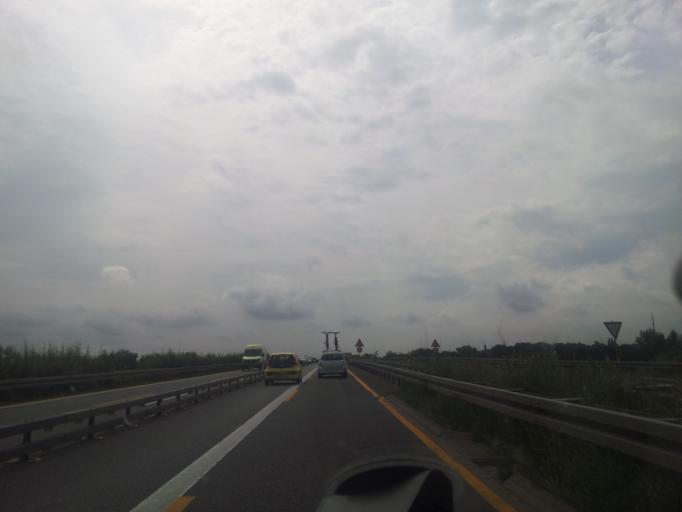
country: DE
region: Saxony-Anhalt
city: Peissen
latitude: 51.5047
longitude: 12.0458
